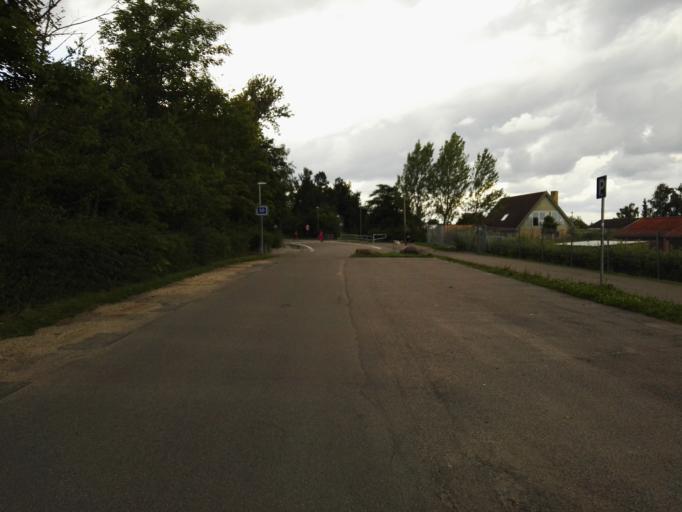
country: DK
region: Capital Region
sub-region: Egedal Kommune
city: Stenlose
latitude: 55.7633
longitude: 12.1995
